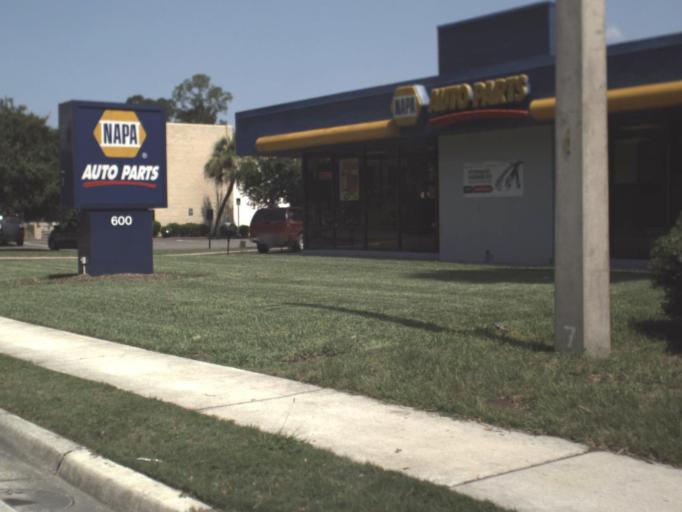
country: US
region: Florida
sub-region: Alachua County
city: Gainesville
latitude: 29.6739
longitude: -82.3185
